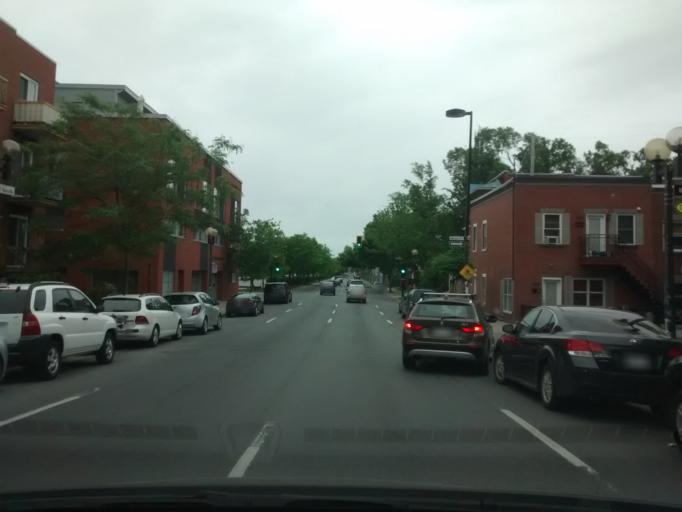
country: CA
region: Quebec
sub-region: Monteregie
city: Longueuil
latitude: 45.5342
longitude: -73.5573
